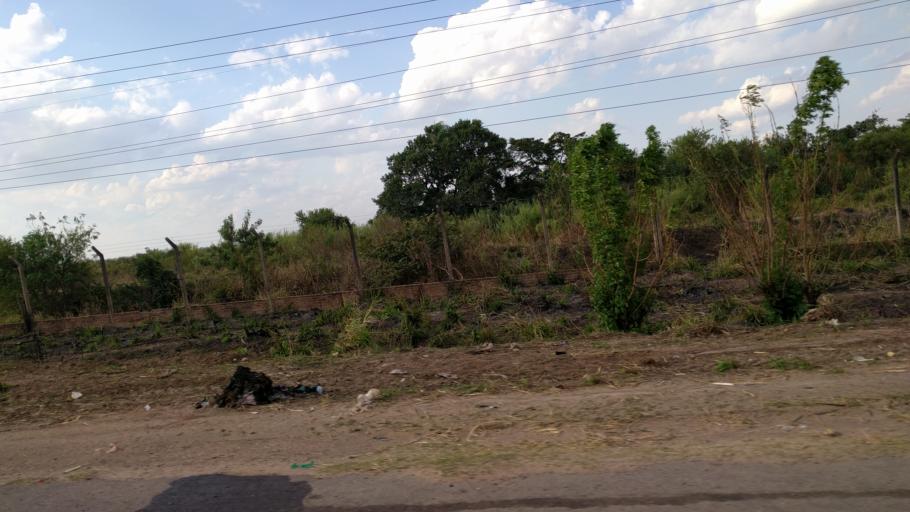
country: BO
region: Santa Cruz
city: Montero
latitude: -17.3712
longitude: -63.2350
